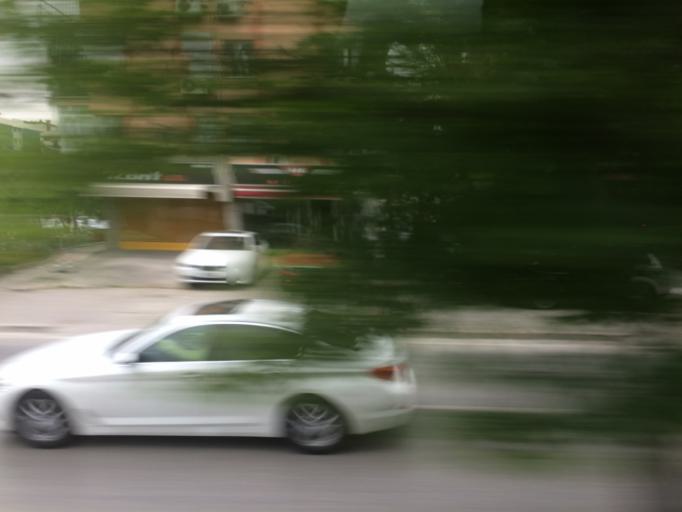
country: TR
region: Izmir
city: Bornova
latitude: 38.4537
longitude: 27.1951
